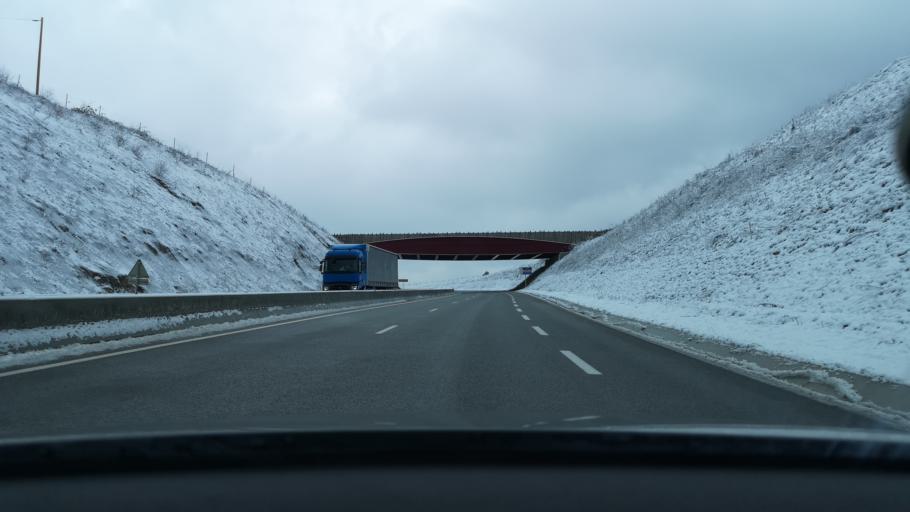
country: FR
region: Rhone-Alpes
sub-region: Departement de l'Ain
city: Dortan
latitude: 46.3197
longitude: 5.6735
